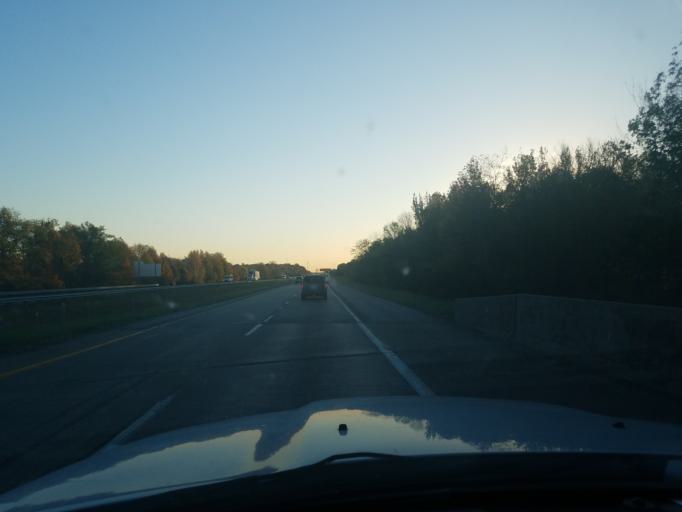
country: US
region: Indiana
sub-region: Clark County
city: Clarksville
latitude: 38.3448
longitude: -85.7837
